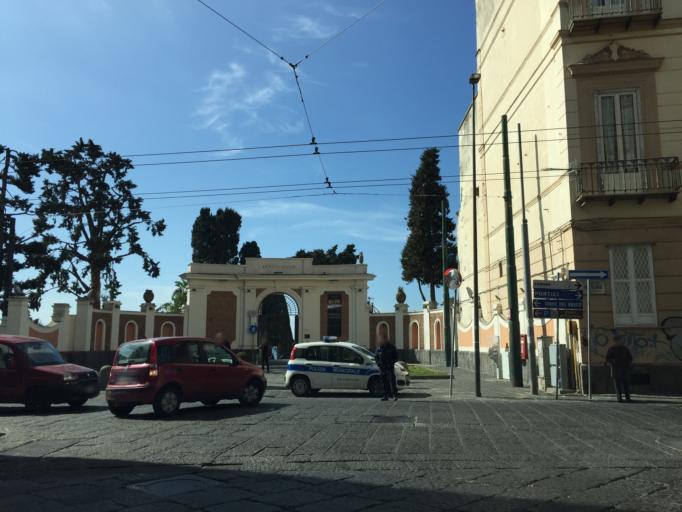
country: IT
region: Campania
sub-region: Provincia di Napoli
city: Portici
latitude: 40.8061
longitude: 14.3495
